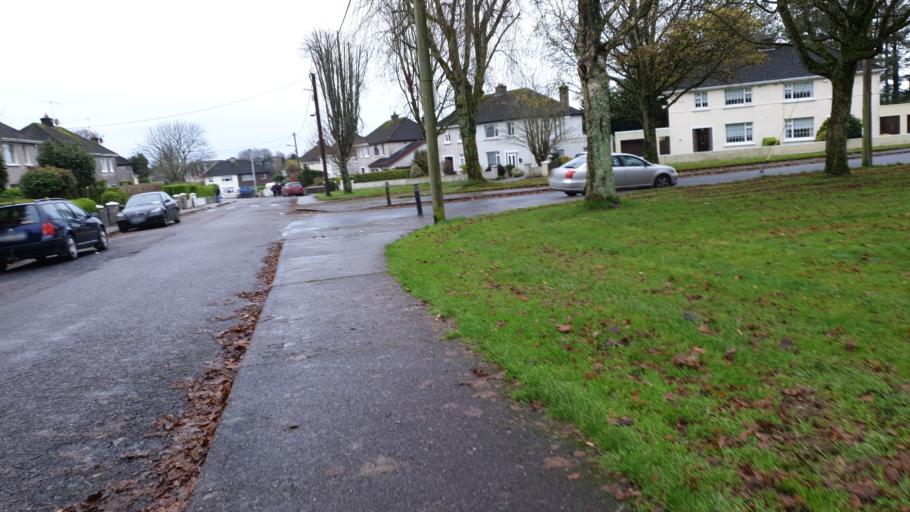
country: IE
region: Munster
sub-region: County Cork
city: Cork
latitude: 51.8896
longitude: -8.4232
